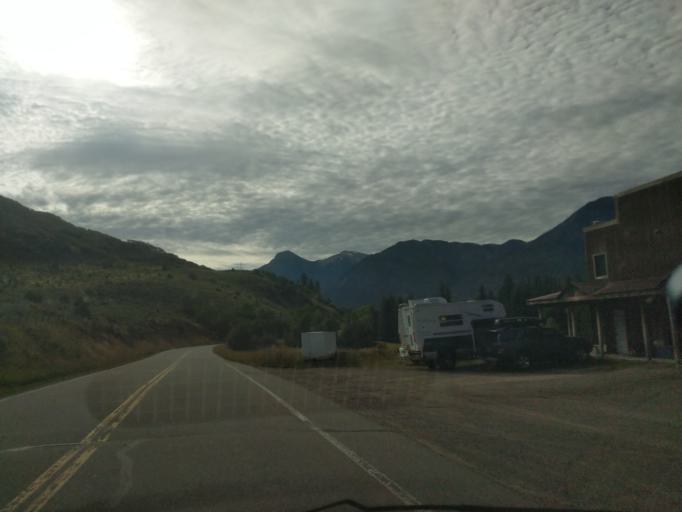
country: US
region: Colorado
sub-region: Garfield County
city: Carbondale
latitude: 39.0852
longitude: -107.2398
